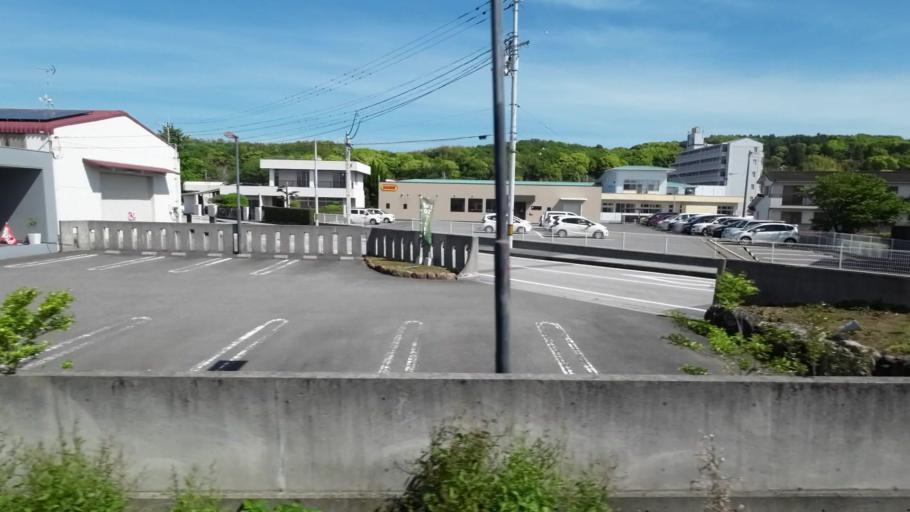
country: JP
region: Kochi
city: Kochi-shi
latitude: 33.5784
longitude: 133.6428
